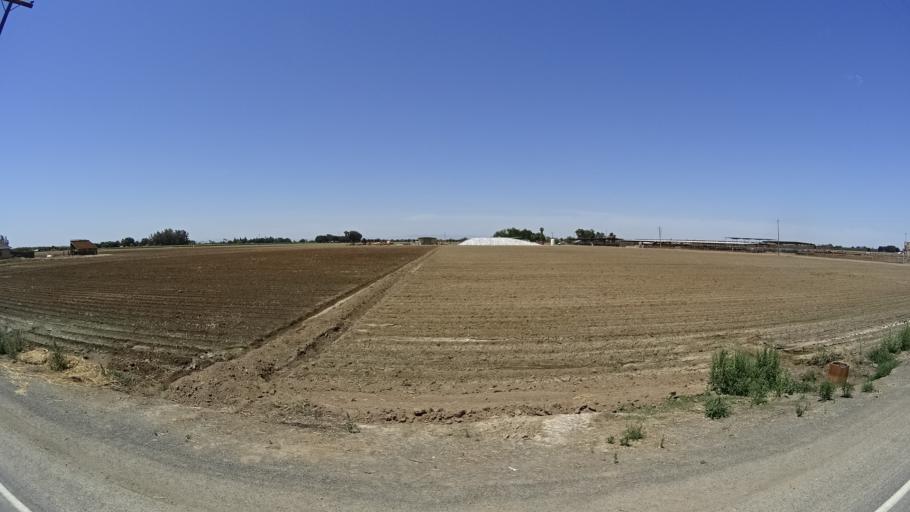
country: US
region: California
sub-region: Kings County
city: Lemoore
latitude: 36.3489
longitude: -119.7808
